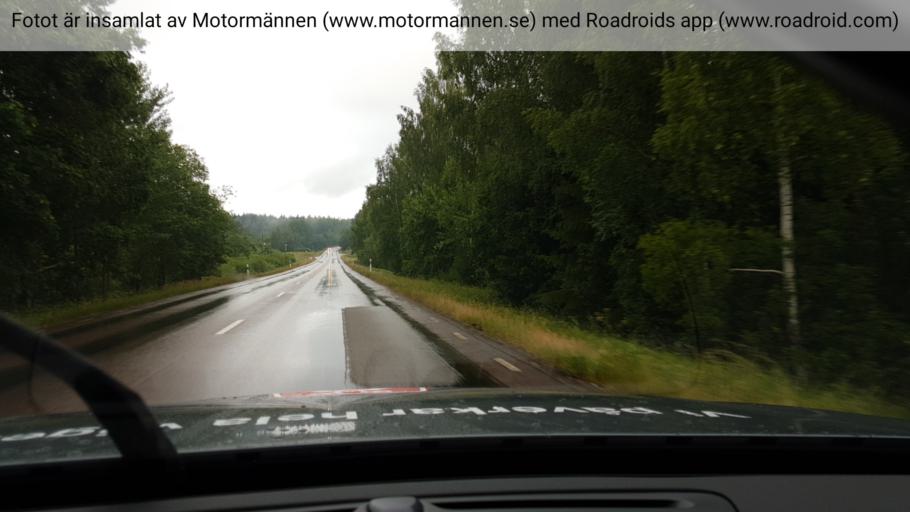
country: SE
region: Vaestmanland
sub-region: Norbergs Kommun
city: Norberg
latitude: 60.0347
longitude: 15.9803
